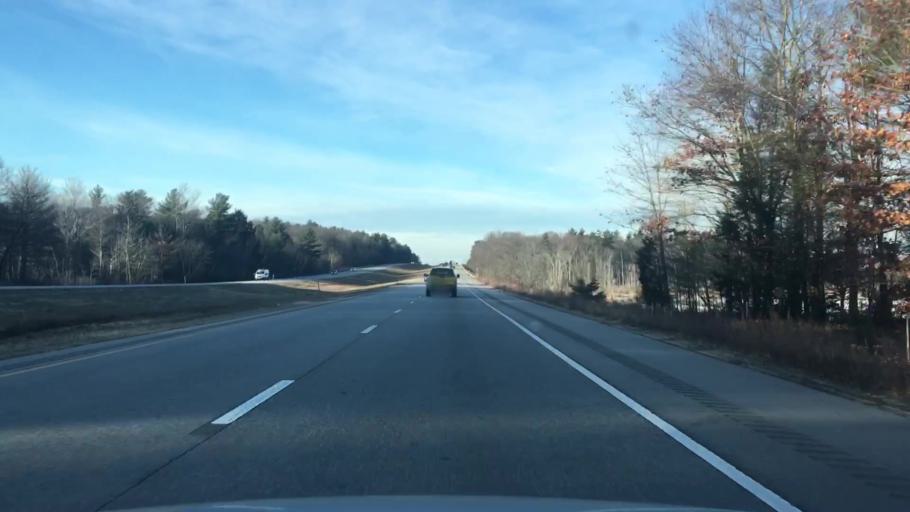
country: US
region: New Hampshire
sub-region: Rockingham County
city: Candia
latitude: 43.0417
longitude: -71.2831
